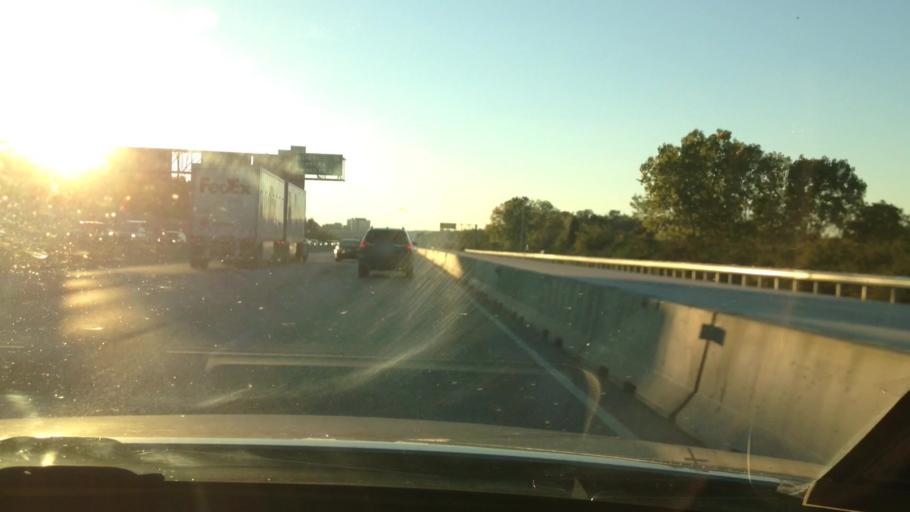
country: US
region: Missouri
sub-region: Jackson County
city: Grandview
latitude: 38.9383
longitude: -94.5493
